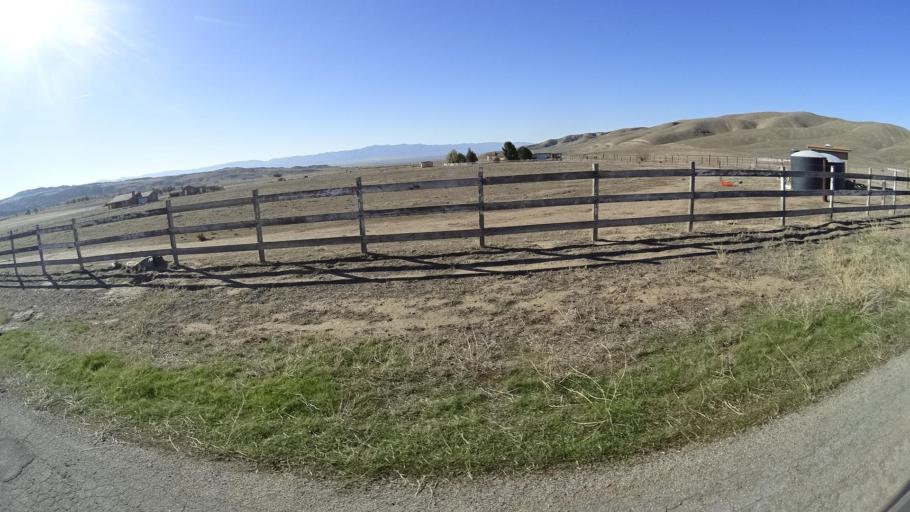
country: US
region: California
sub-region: Kern County
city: Maricopa
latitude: 34.9428
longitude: -119.4554
